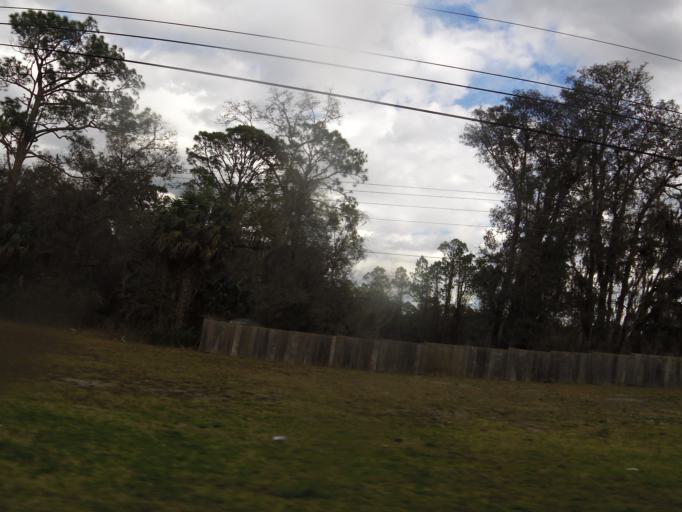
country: US
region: Florida
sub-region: Volusia County
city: Pierson
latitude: 29.2768
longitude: -81.4760
